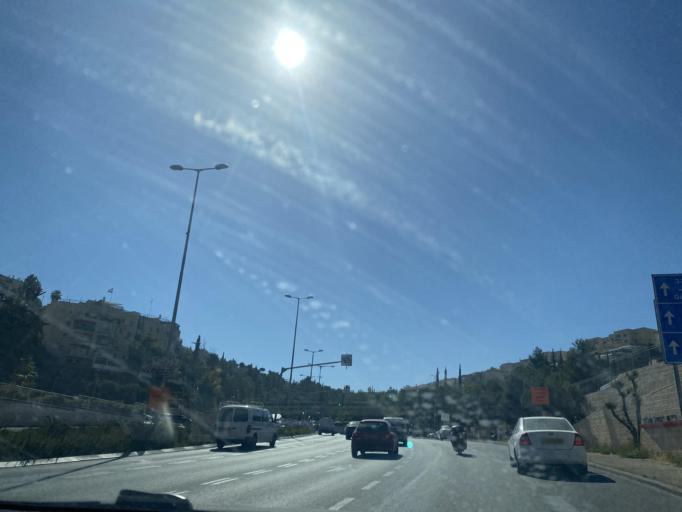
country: PS
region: West Bank
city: Bayt Iksa
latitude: 31.8123
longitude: 35.2021
